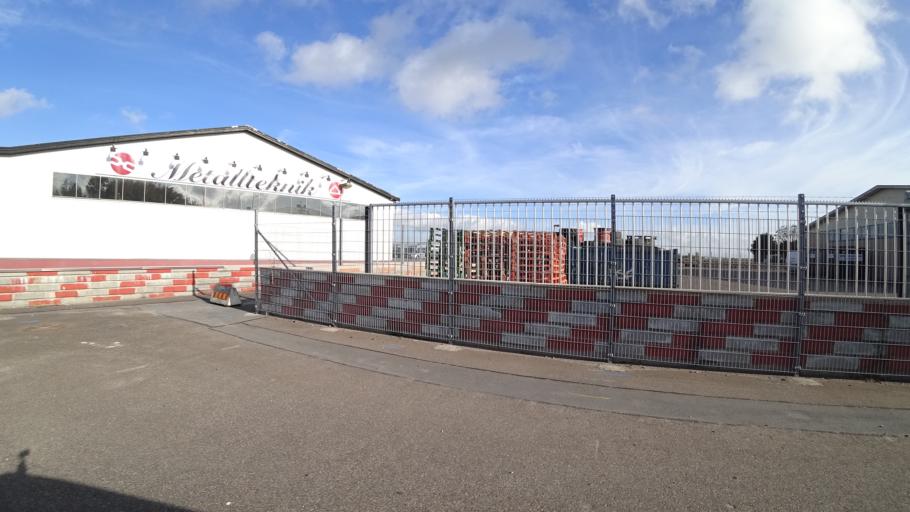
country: SE
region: Skane
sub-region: Staffanstorps Kommun
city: Staffanstorp
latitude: 55.6587
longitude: 13.2301
